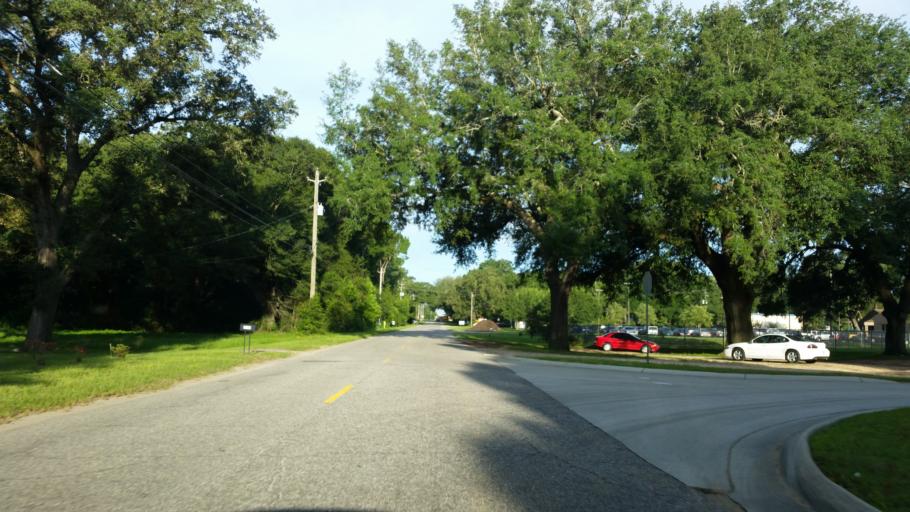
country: US
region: Florida
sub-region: Escambia County
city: Bellview
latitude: 30.4757
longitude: -87.3025
